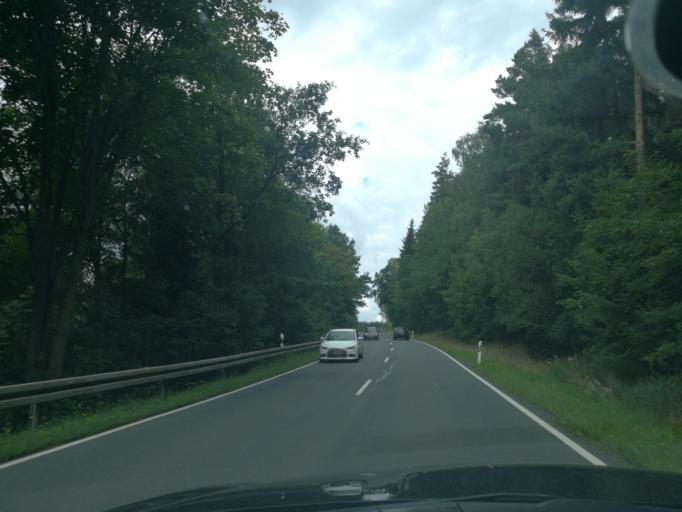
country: DE
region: Saxony
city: Adorf
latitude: 50.3597
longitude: 12.2256
